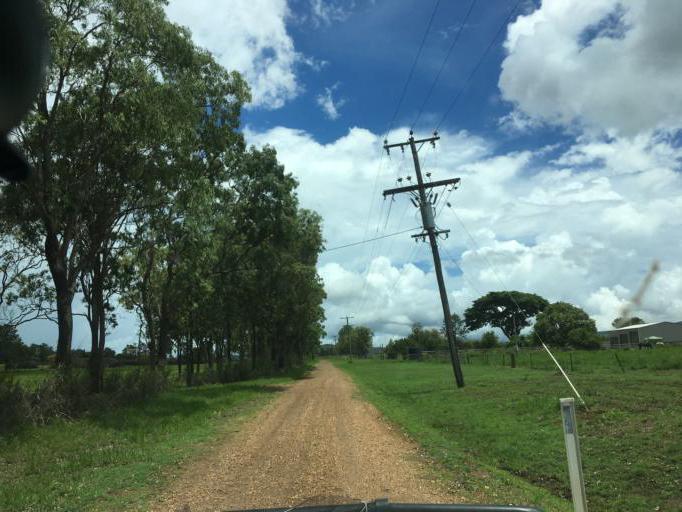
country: AU
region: Queensland
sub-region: Tablelands
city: Mareeba
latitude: -16.9923
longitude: 145.5217
